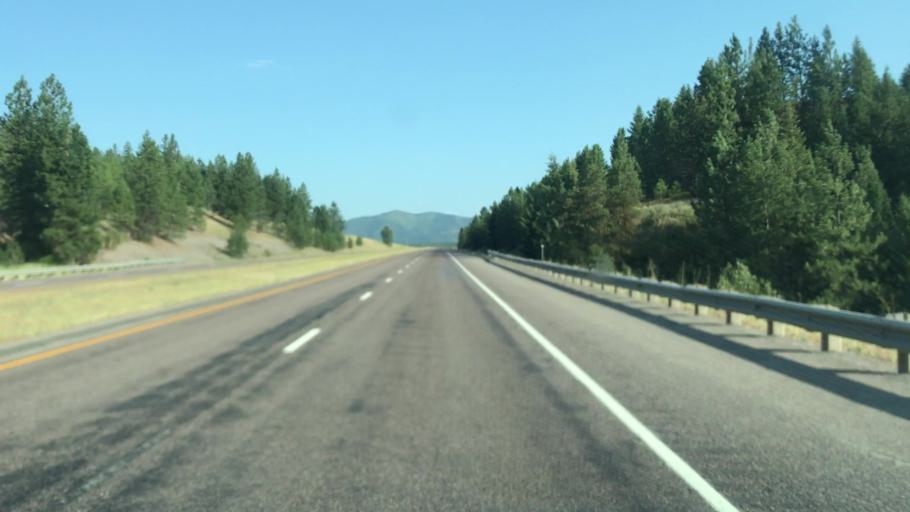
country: US
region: Montana
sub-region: Mineral County
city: Superior
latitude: 47.0528
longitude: -114.7585
